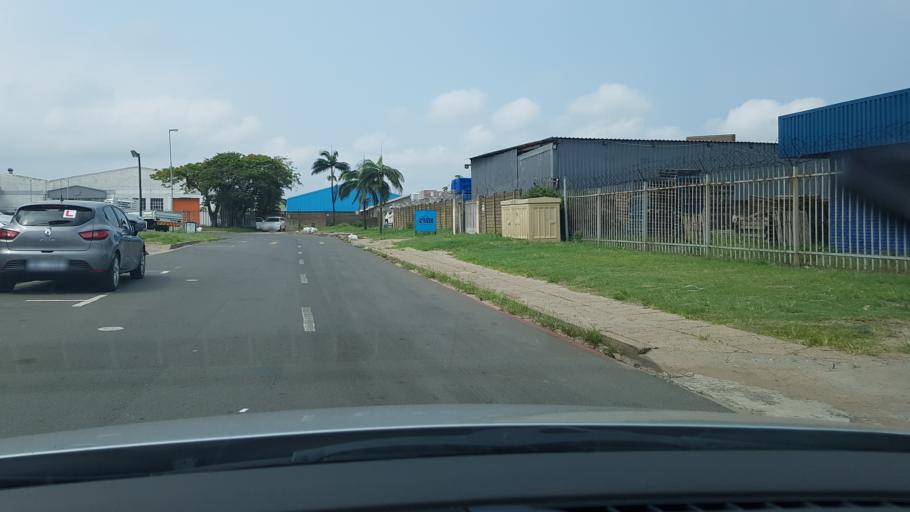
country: ZA
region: KwaZulu-Natal
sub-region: uThungulu District Municipality
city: Richards Bay
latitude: -28.7522
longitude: 32.0464
